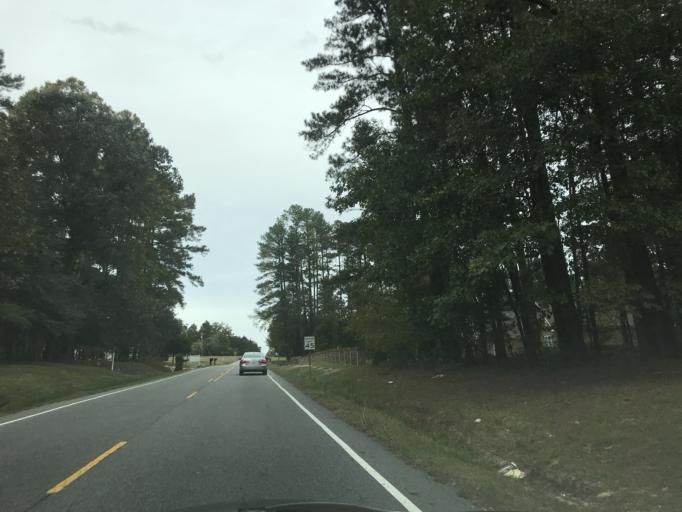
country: US
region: North Carolina
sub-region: Wake County
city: Rolesville
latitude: 35.9189
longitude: -78.5055
